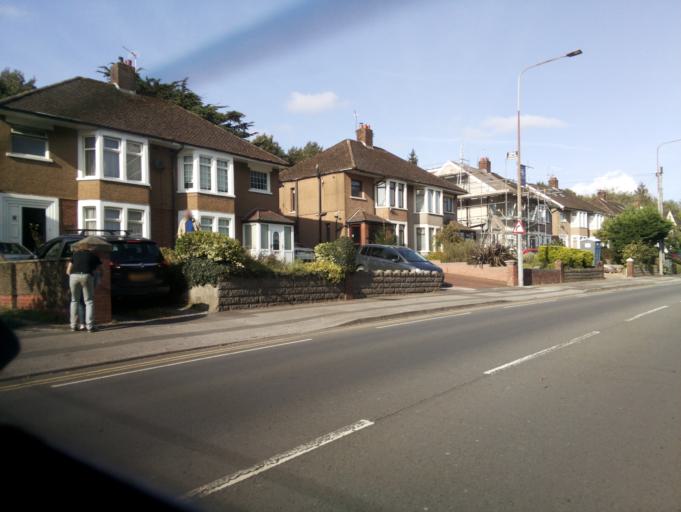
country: GB
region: Wales
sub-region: Caerphilly County Borough
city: Caerphilly
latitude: 51.5280
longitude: -3.1979
